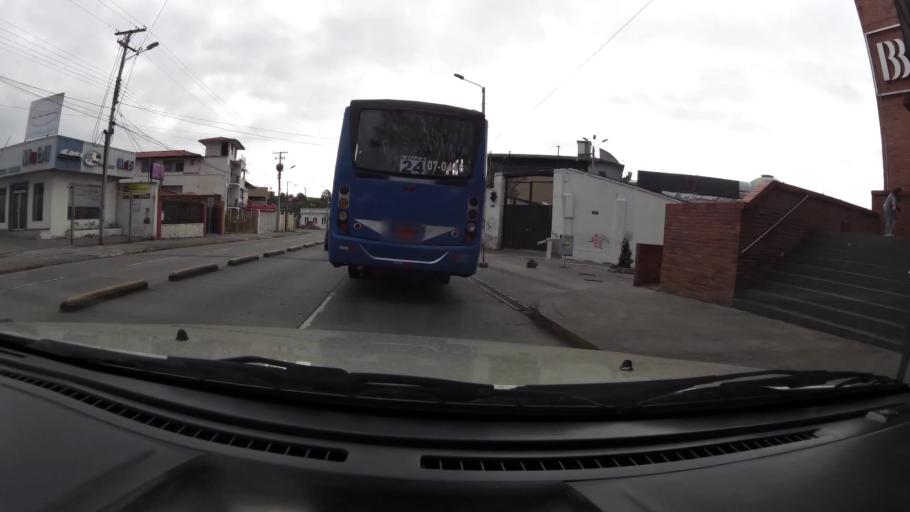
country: EC
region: Azuay
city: Cuenca
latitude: -2.9054
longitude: -79.0032
